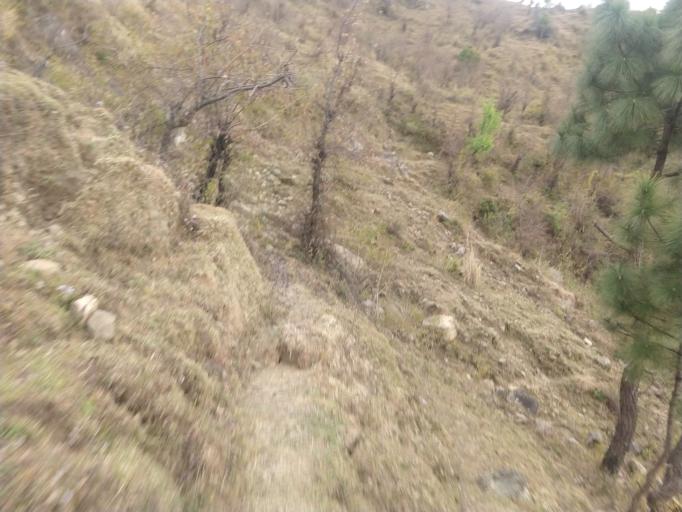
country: IN
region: Himachal Pradesh
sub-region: Kangra
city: Dharmsala
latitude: 32.2201
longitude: 76.3337
